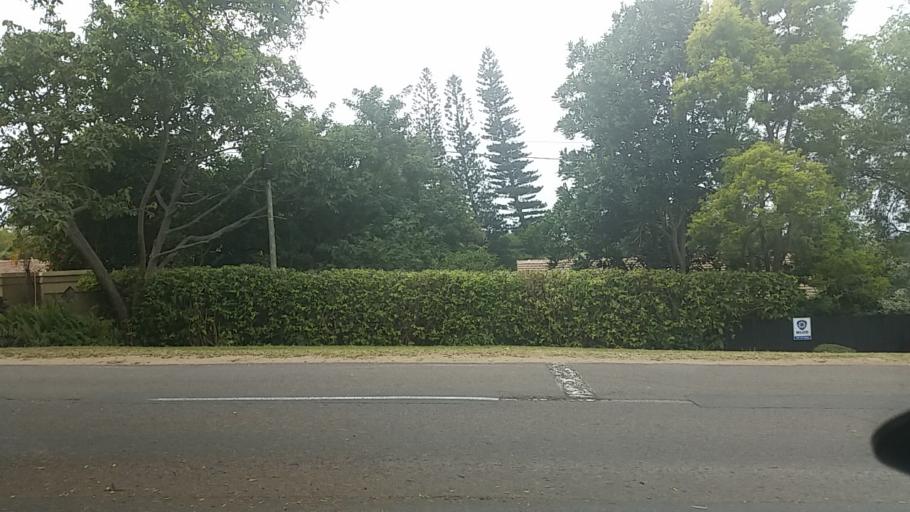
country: ZA
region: KwaZulu-Natal
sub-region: eThekwini Metropolitan Municipality
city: Berea
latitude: -29.8417
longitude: 30.9404
